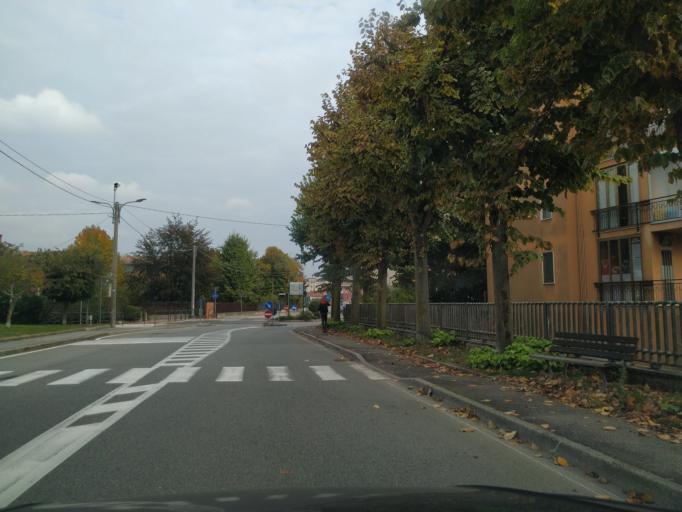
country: IT
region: Piedmont
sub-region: Provincia di Torino
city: Chivasso
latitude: 45.1963
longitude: 7.8852
